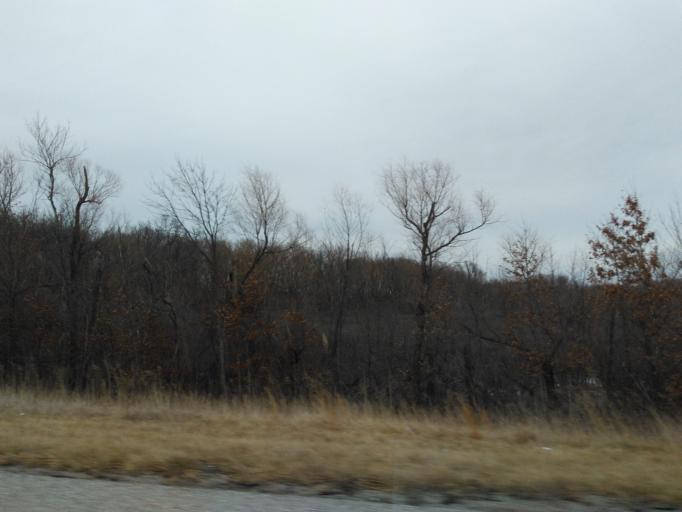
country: US
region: Illinois
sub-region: Clinton County
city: Albers
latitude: 38.4966
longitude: -89.6036
